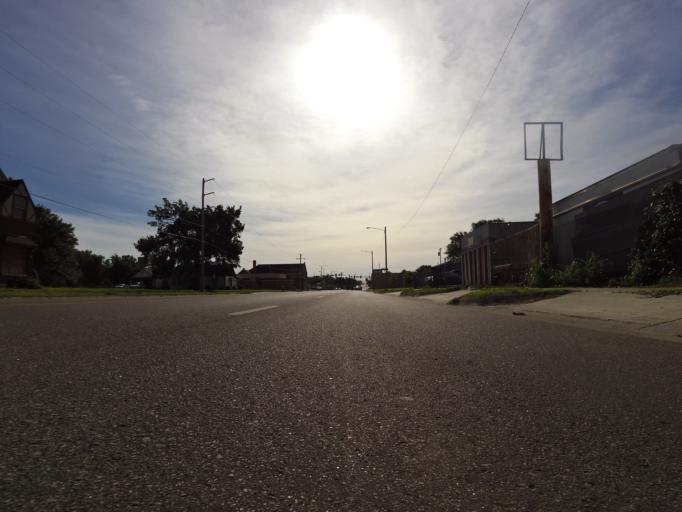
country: US
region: Kansas
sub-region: Sedgwick County
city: Wichita
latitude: 37.7080
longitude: -97.3100
